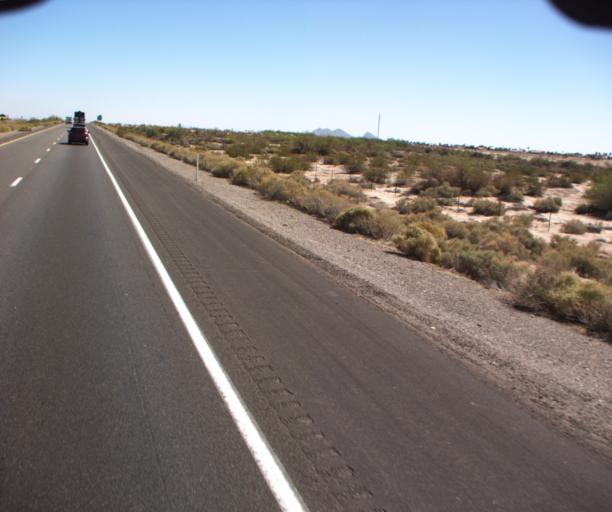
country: US
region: Arizona
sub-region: Yuma County
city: Wellton
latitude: 32.6577
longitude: -114.1594
